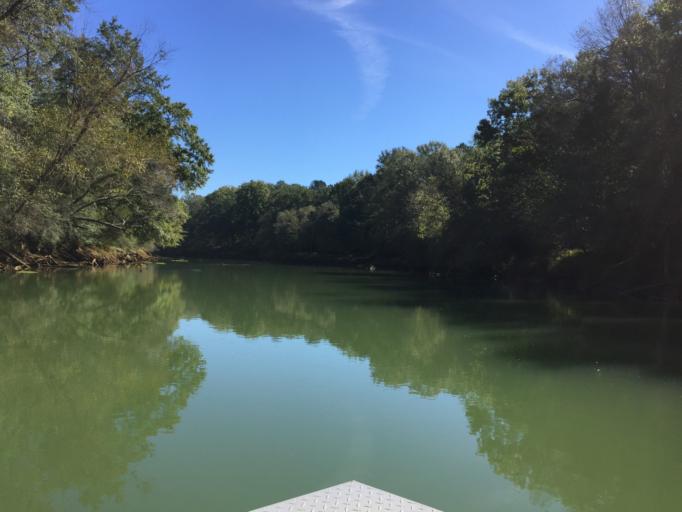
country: US
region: Georgia
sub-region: Gwinnett County
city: Duluth
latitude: 34.0333
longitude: -84.1256
